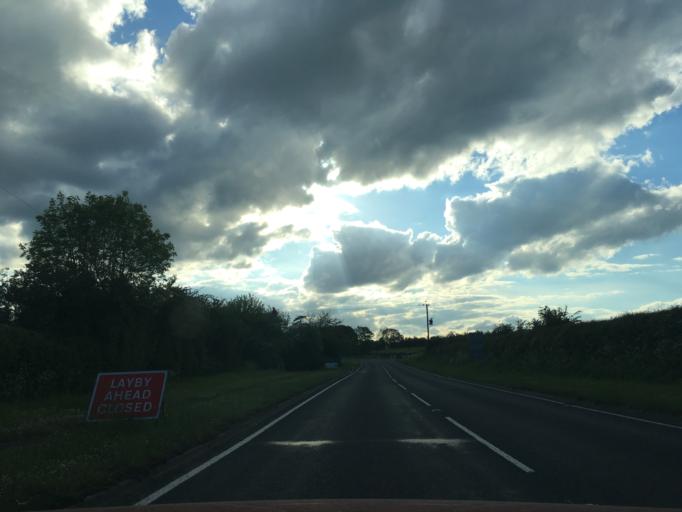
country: GB
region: England
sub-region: Worcestershire
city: Pershore
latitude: 52.1881
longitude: -2.1045
